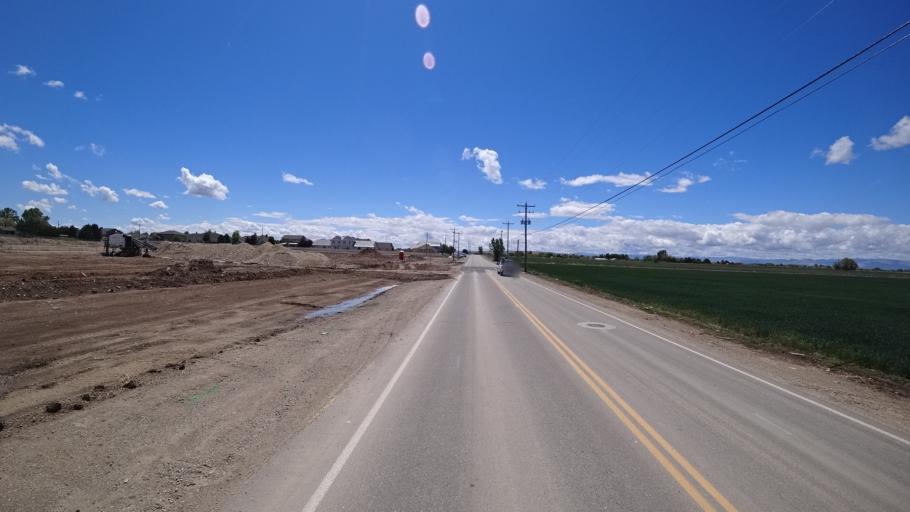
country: US
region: Idaho
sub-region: Ada County
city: Kuna
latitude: 43.5152
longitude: -116.4337
